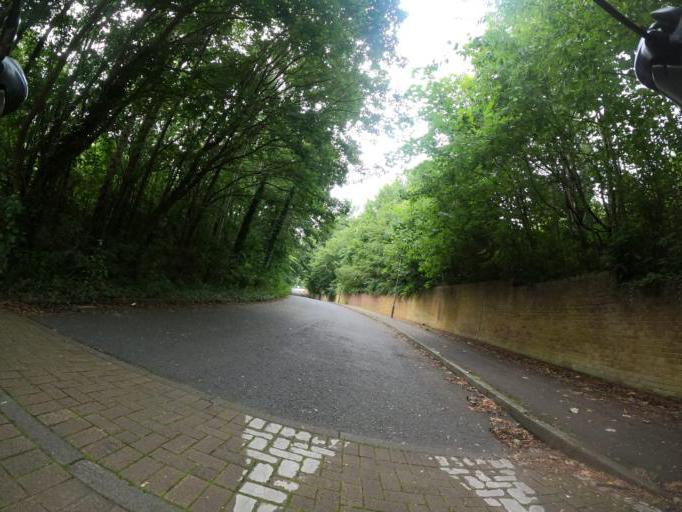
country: GB
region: Scotland
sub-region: East Lothian
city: Musselburgh
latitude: 55.9431
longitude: -3.0934
